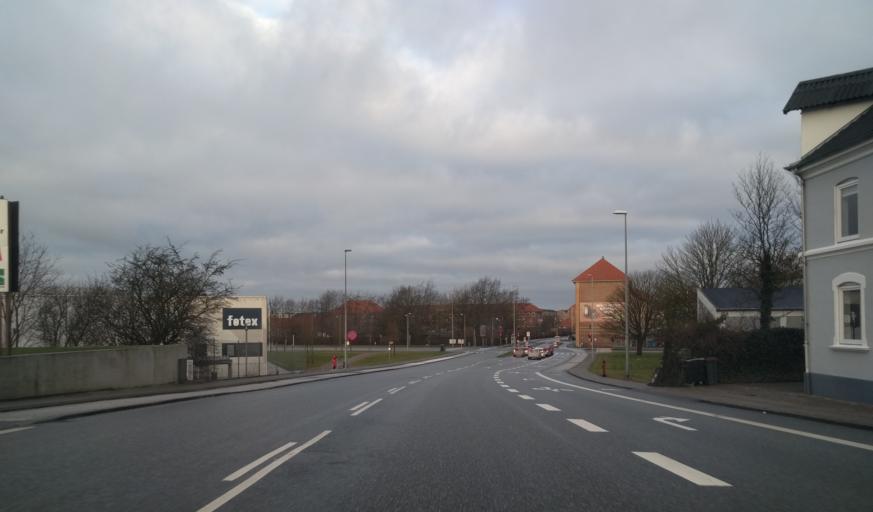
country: DK
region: North Denmark
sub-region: Alborg Kommune
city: Aalborg
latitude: 57.0370
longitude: 9.9370
